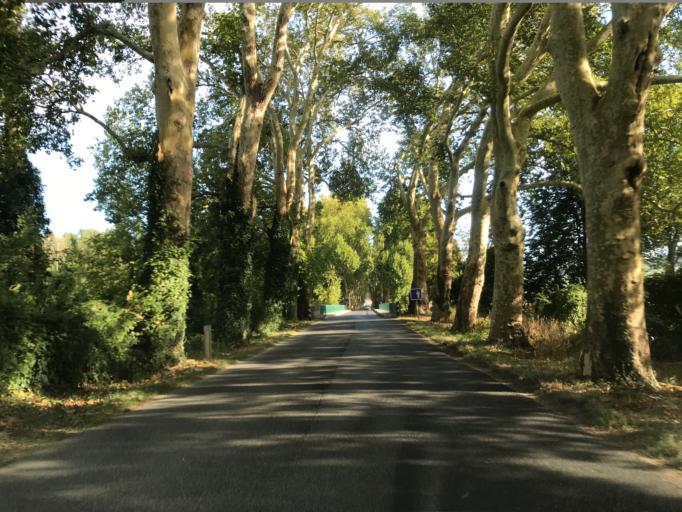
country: FR
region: Champagne-Ardenne
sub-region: Departement de la Marne
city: Damery
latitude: 49.0629
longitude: 3.8744
